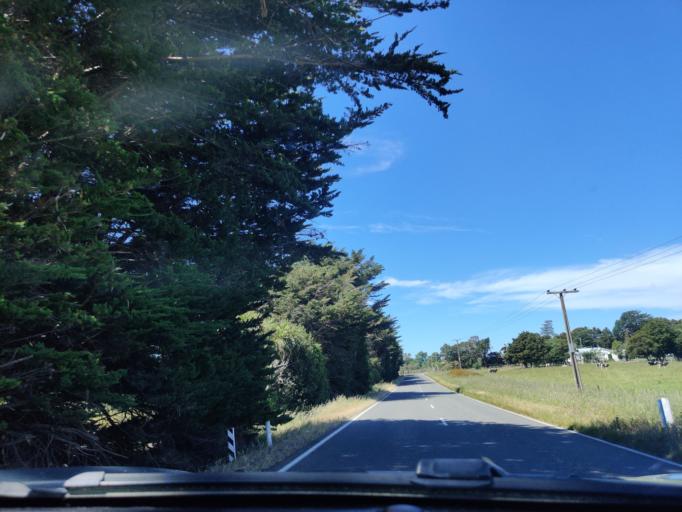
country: NZ
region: Wellington
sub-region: Upper Hutt City
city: Upper Hutt
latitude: -41.3210
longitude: 175.2506
